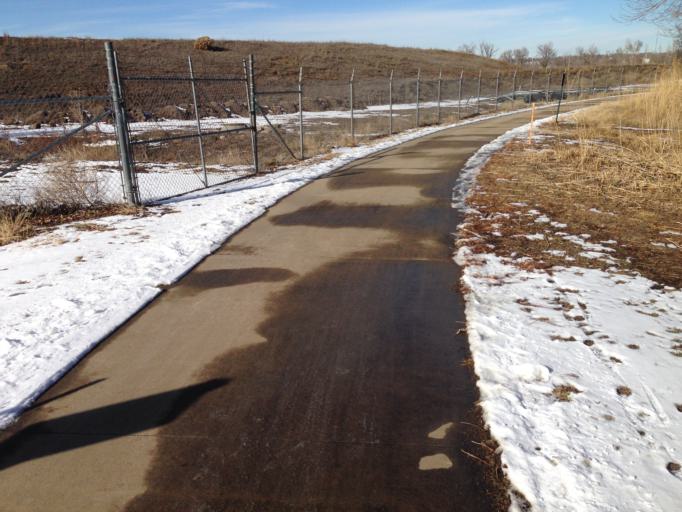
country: US
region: Colorado
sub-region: Adams County
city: Berkley
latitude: 39.8006
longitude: -105.0310
